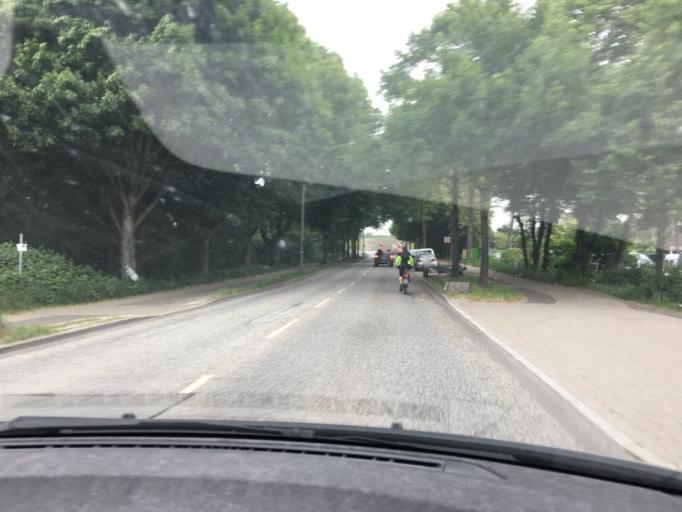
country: DE
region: Hamburg
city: Kleiner Grasbrook
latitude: 53.5171
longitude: 9.9936
